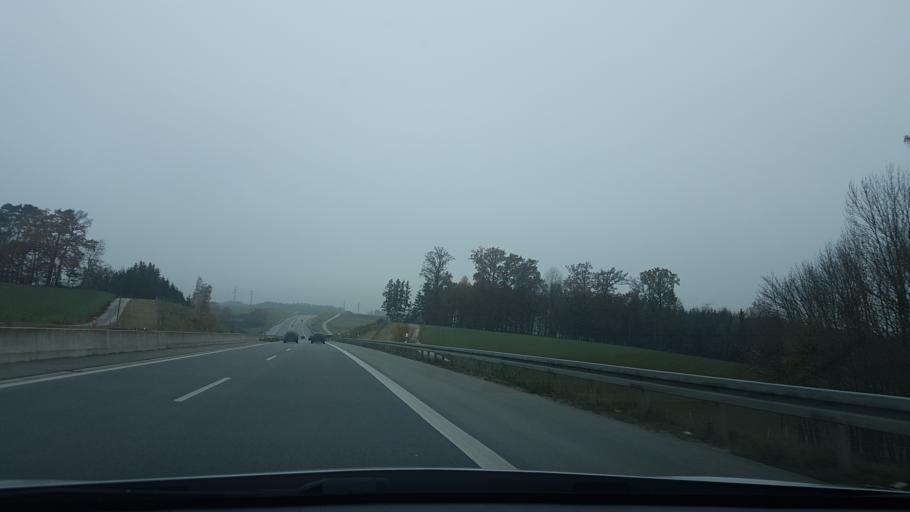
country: DE
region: Bavaria
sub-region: Lower Bavaria
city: Ergoldsbach
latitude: 48.6822
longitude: 12.1882
